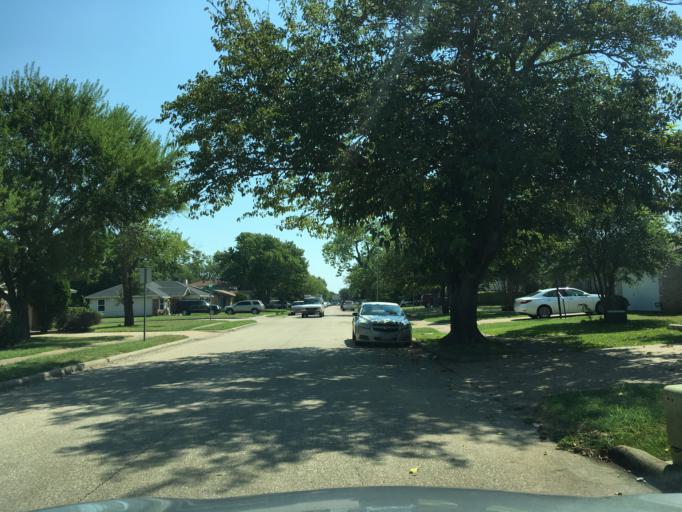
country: US
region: Texas
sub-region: Dallas County
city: Garland
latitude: 32.9382
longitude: -96.6532
